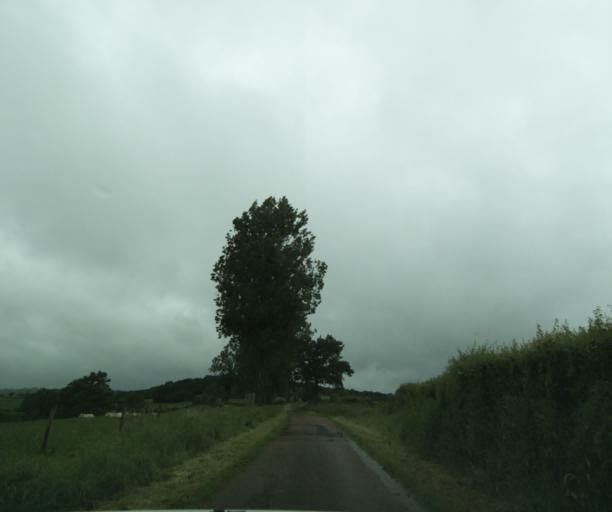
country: FR
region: Bourgogne
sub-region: Departement de Saone-et-Loire
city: Charolles
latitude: 46.3857
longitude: 4.2200
